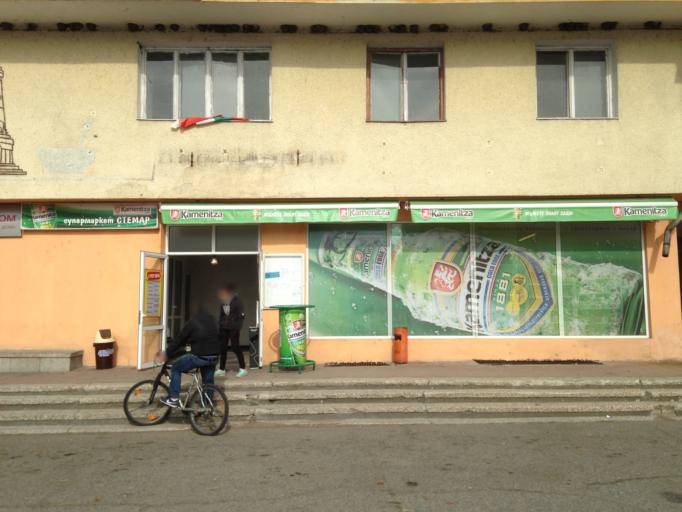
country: BG
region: Stara Zagora
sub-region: Obshtina Kazanluk
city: Shipka
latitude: 42.7124
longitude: 25.3326
